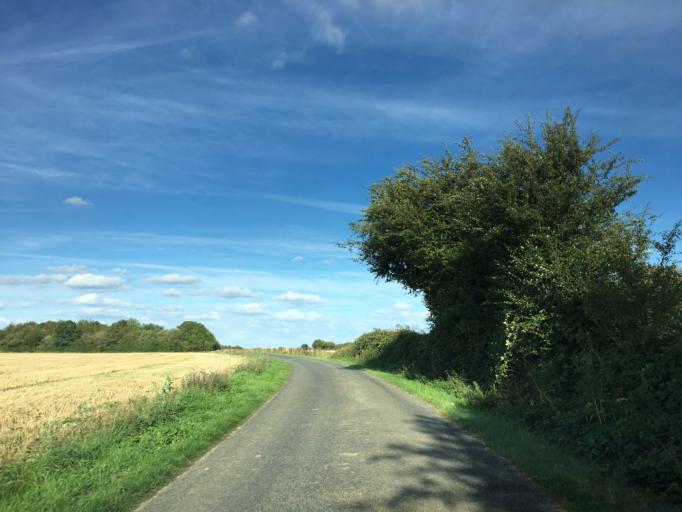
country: FR
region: Lower Normandy
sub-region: Departement de l'Orne
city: Aube-sur-Rile
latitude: 48.8626
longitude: 0.4762
